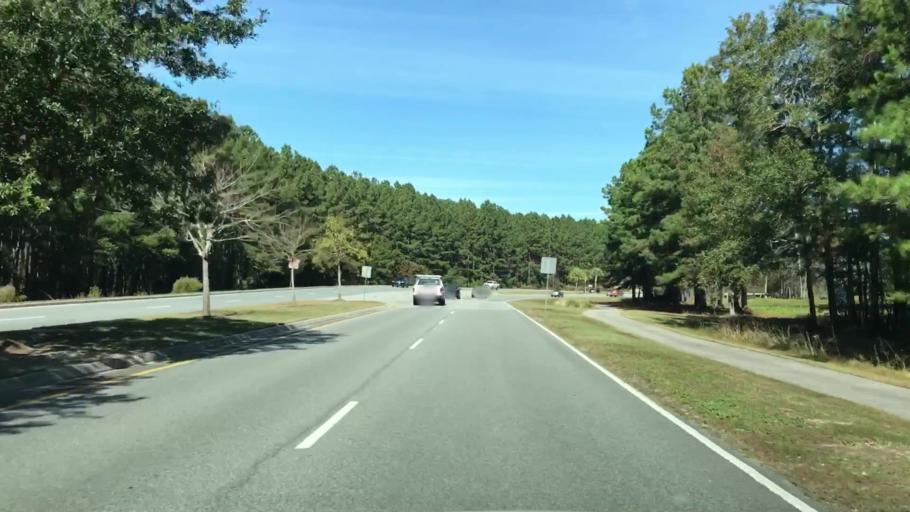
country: US
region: South Carolina
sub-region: Beaufort County
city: Bluffton
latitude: 32.2776
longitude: -80.9133
